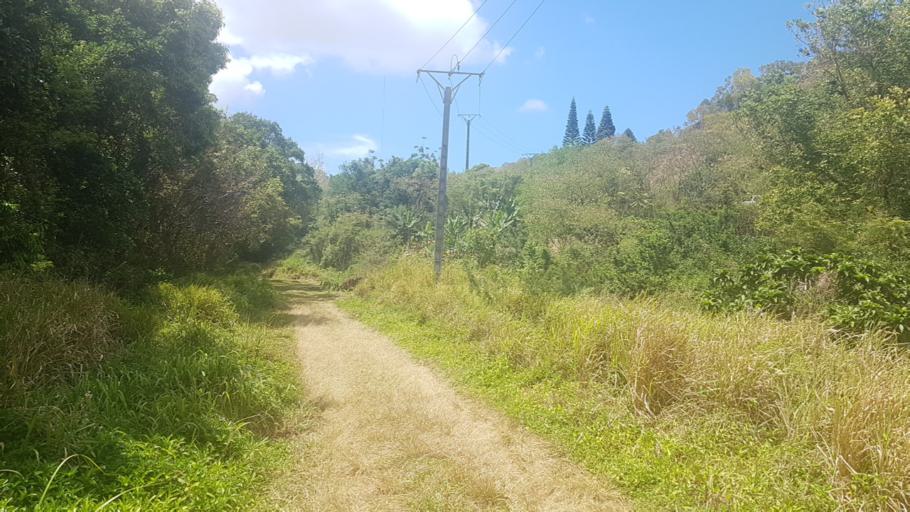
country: NC
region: South Province
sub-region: Dumbea
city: Dumbea
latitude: -22.1872
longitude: 166.4799
